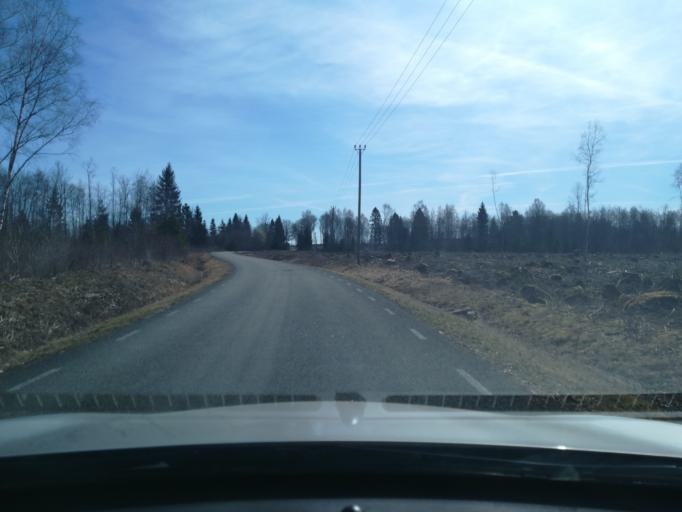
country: EE
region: Harju
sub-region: Saku vald
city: Saku
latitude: 59.2946
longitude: 24.6134
